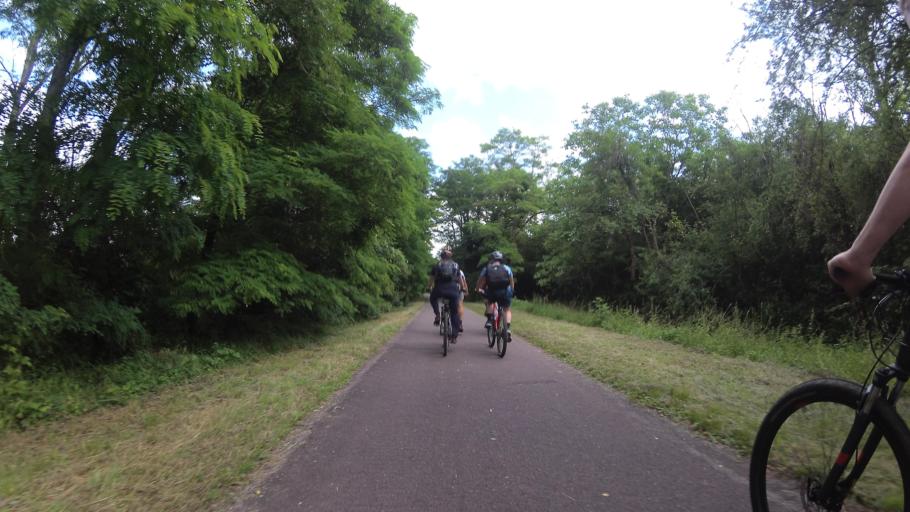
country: FR
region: Lorraine
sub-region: Departement de la Moselle
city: Bliesbruck
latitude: 49.1134
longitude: 7.1699
